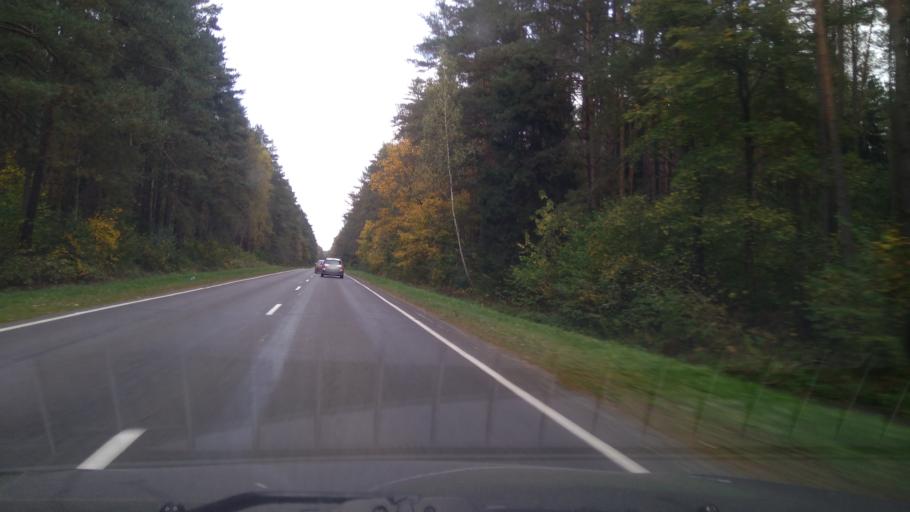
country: BY
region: Minsk
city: Druzhny
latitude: 53.6273
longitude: 27.8751
